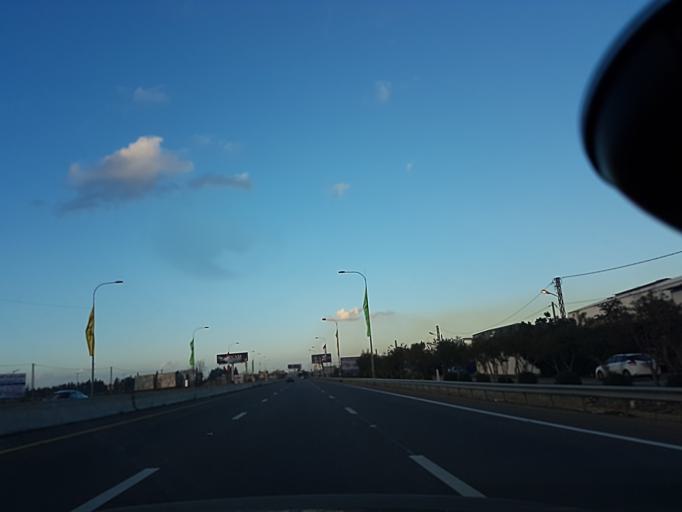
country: LB
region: Liban-Sud
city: Sidon
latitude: 33.5218
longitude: 35.3640
